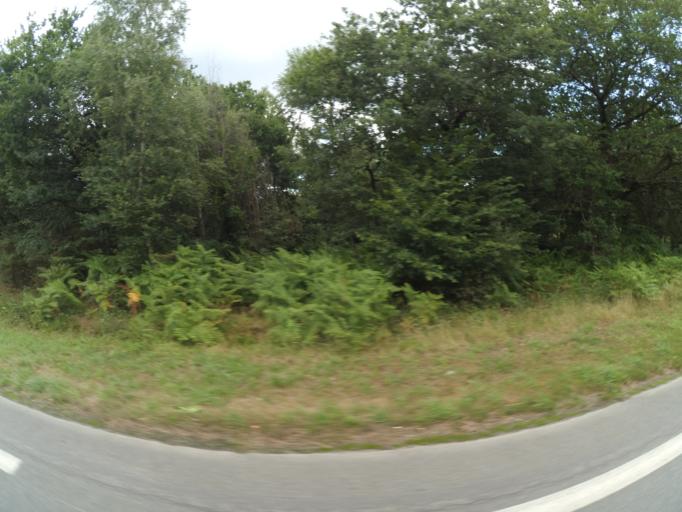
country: FR
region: Brittany
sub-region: Departement du Morbihan
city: Merlevenez
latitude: 47.7457
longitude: -3.2265
